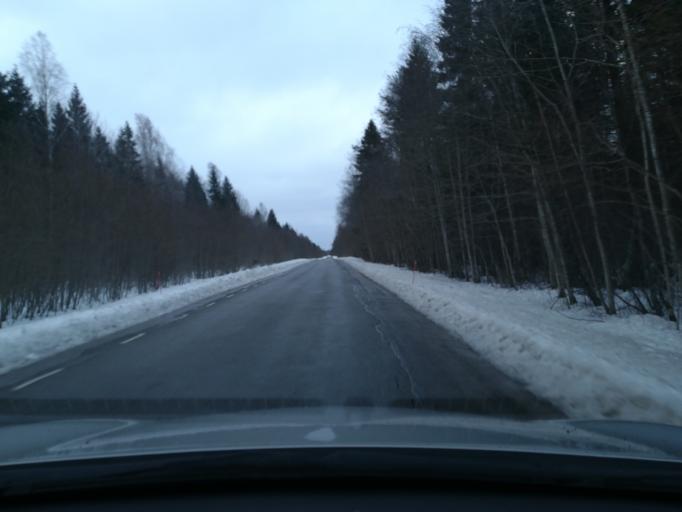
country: EE
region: Harju
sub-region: Nissi vald
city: Turba
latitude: 59.0700
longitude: 24.2499
